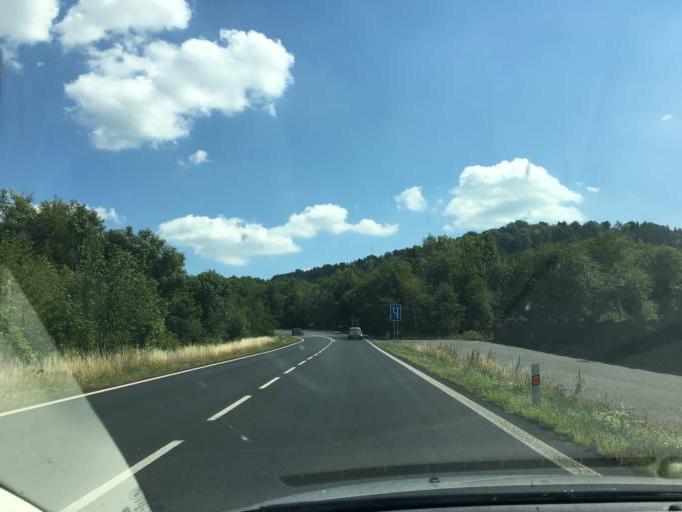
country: CZ
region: Ustecky
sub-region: Okres Decin
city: Decin
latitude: 50.7890
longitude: 14.2657
